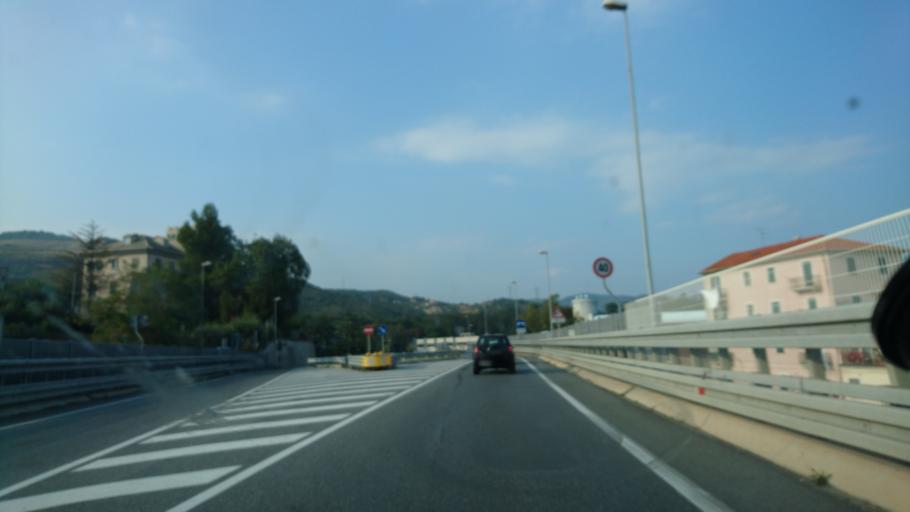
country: IT
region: Liguria
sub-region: Provincia di Savona
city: Vado Centro
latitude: 44.2661
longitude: 8.4253
